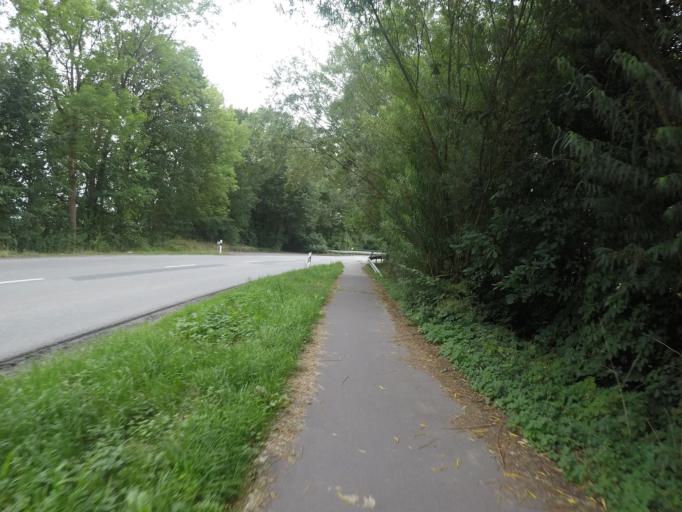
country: DE
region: Lower Saxony
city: Grossenworden
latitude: 53.6555
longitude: 9.2940
